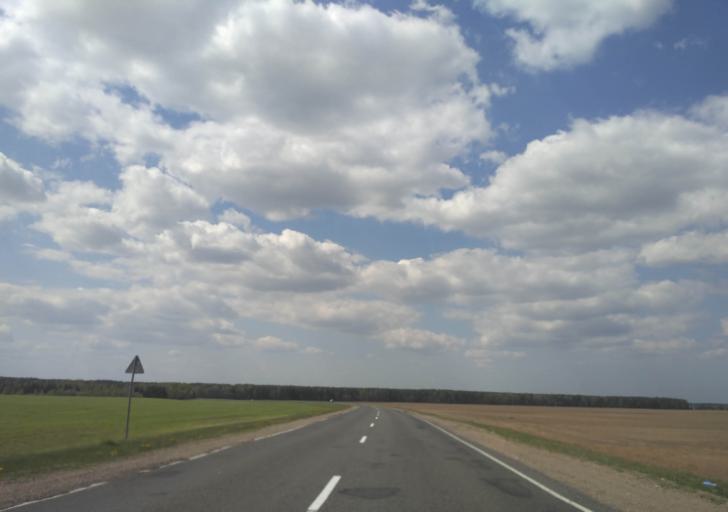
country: BY
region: Minsk
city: Vilyeyka
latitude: 54.5175
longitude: 27.0290
